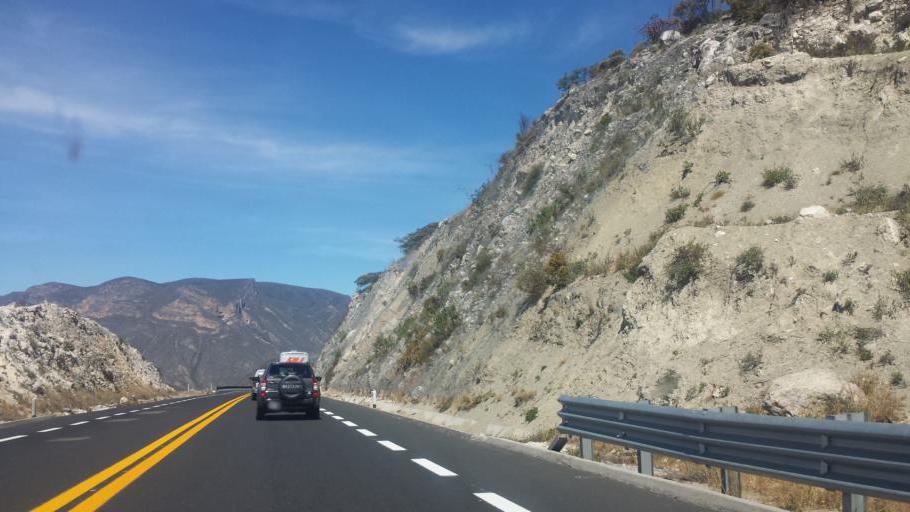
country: MX
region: Puebla
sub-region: San Jose Miahuatlan
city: San Pedro Tetitlan
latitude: 18.0837
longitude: -97.3508
